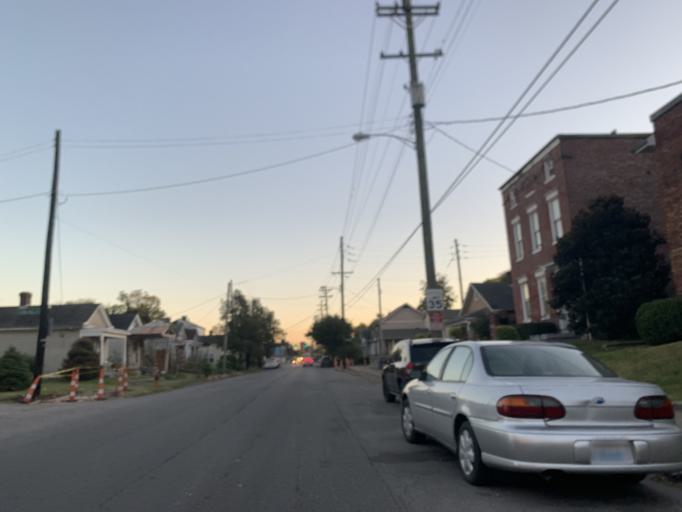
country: US
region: Kentucky
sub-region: Jefferson County
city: Louisville
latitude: 38.2380
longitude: -85.7782
